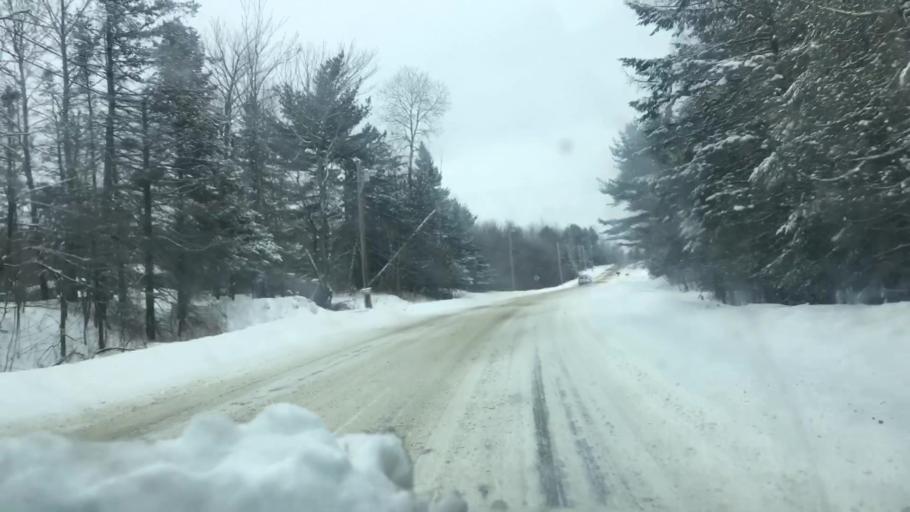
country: US
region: Maine
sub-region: Penobscot County
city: Bradford
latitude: 45.0321
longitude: -68.9484
